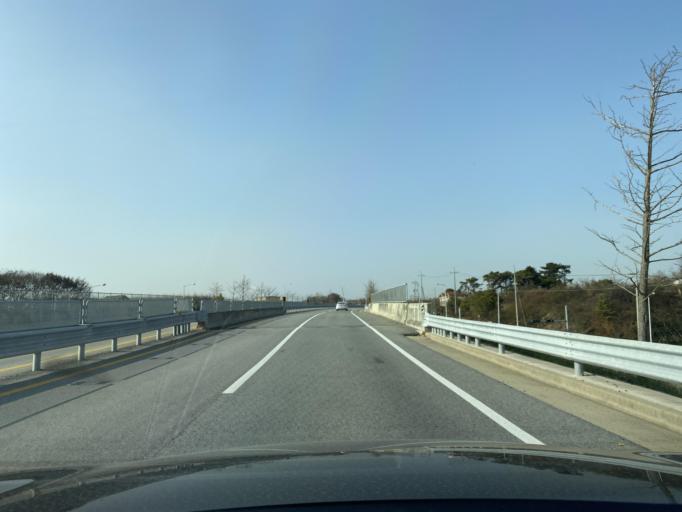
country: KR
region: Chungcheongnam-do
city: Yesan
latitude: 36.7578
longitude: 126.8210
